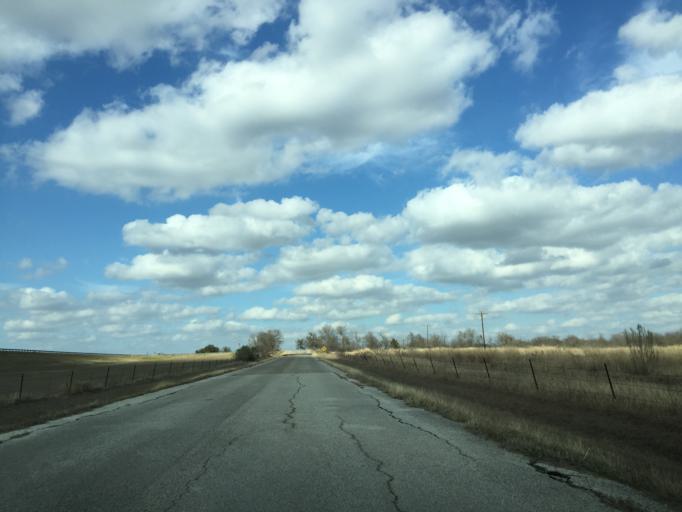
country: US
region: Texas
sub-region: Williamson County
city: Granger
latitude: 30.7141
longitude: -97.3223
